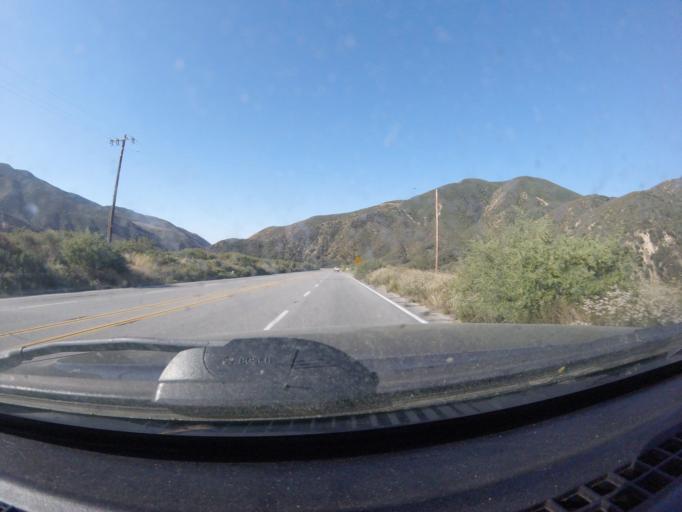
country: US
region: California
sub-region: San Bernardino County
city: Highland
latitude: 34.1803
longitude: -117.1844
